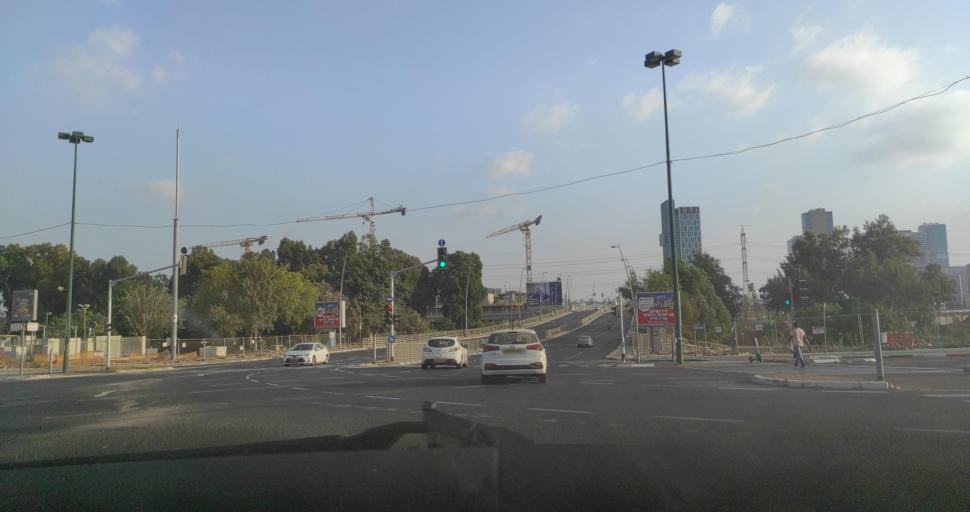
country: IL
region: Tel Aviv
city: Bene Beraq
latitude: 32.1073
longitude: 34.8272
